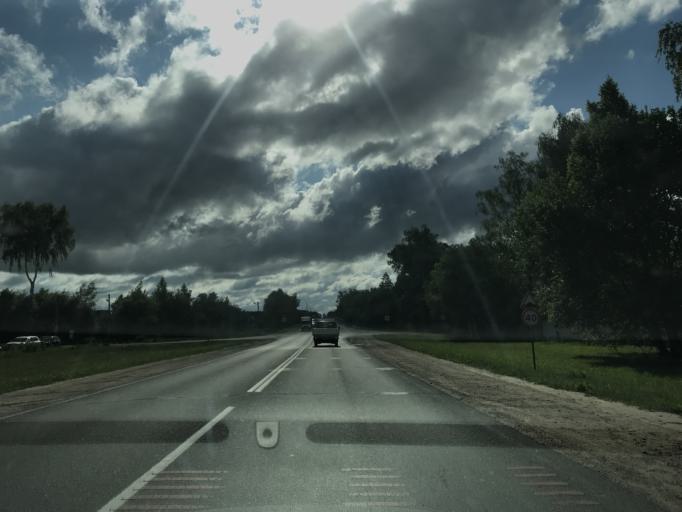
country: BY
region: Minsk
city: Borovlyany
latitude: 53.9673
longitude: 27.6372
